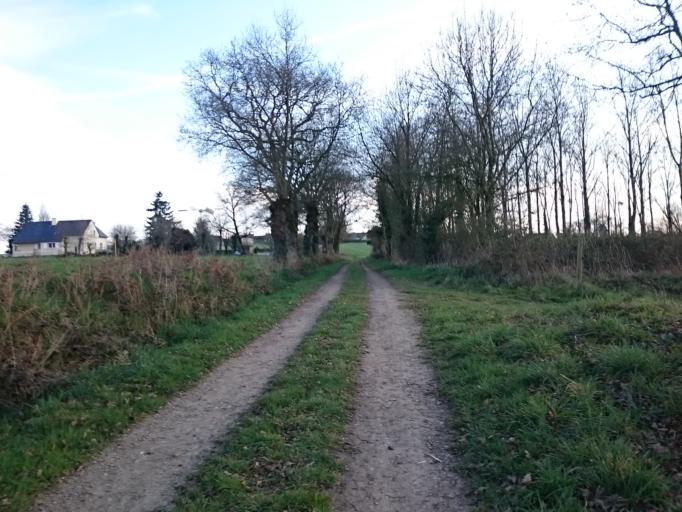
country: FR
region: Brittany
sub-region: Departement d'Ille-et-Vilaine
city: Chanteloup
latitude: 47.9311
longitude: -1.6088
